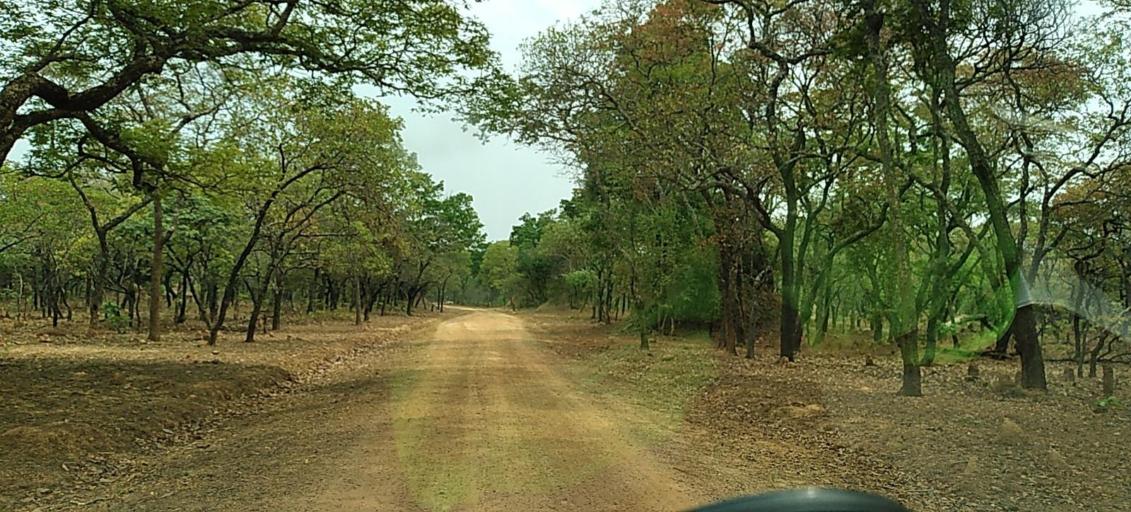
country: ZM
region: North-Western
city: Solwezi
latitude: -12.9283
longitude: 26.5608
